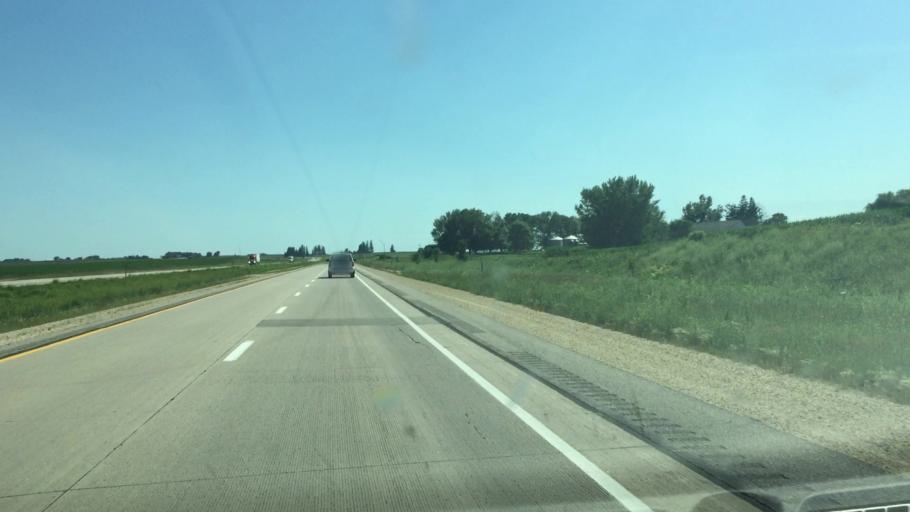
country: US
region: Iowa
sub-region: Jones County
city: Monticello
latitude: 42.1879
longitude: -91.2191
